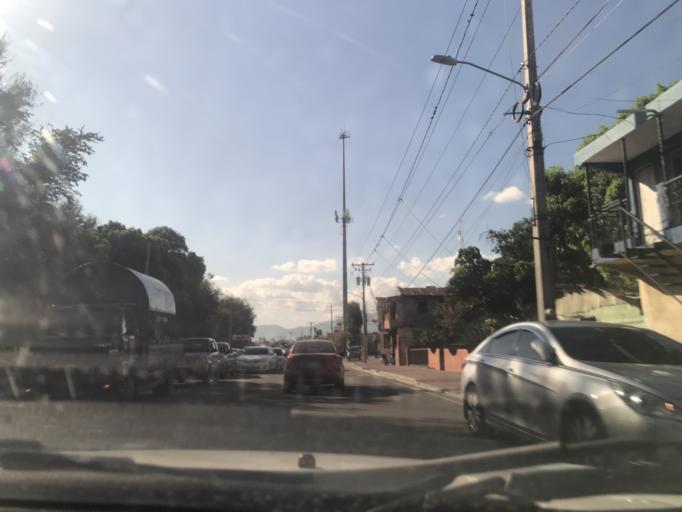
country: DO
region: Santiago
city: Santiago de los Caballeros
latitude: 19.4360
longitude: -70.6974
